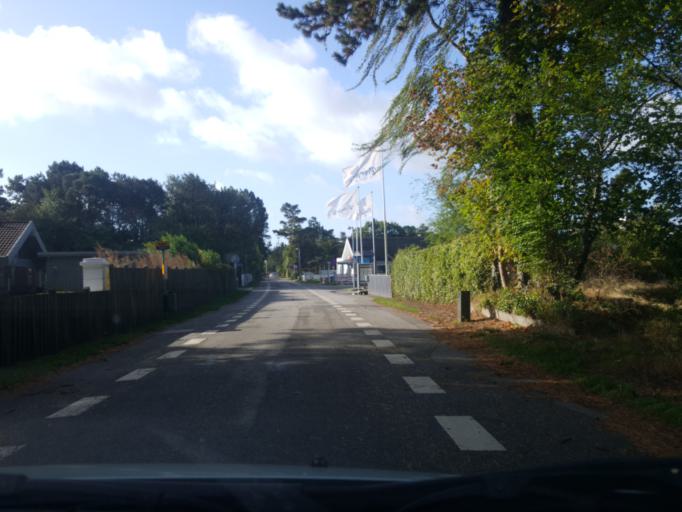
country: DK
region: Zealand
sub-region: Guldborgsund Kommune
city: Nykobing Falster
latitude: 54.6777
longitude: 11.9604
